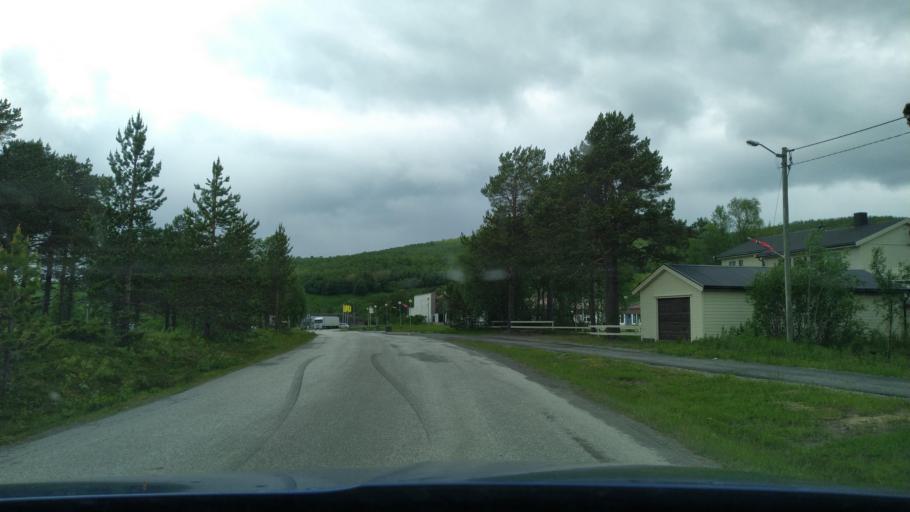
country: NO
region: Troms
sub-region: Dyroy
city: Brostadbotn
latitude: 69.0901
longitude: 17.7002
